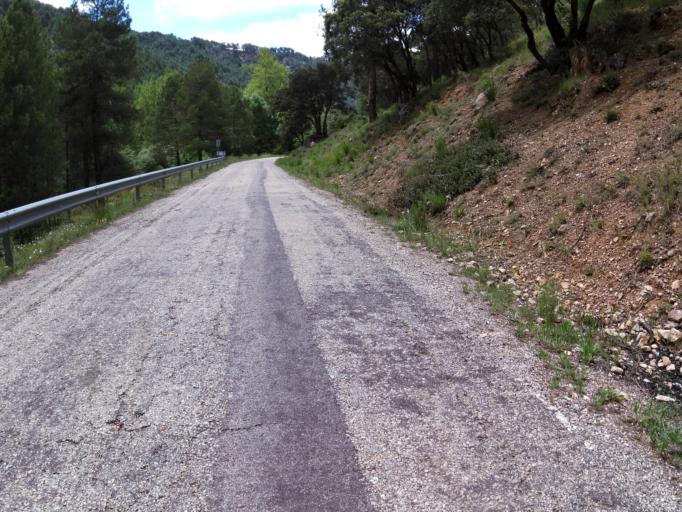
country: ES
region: Castille-La Mancha
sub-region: Provincia de Albacete
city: Paterna del Madera
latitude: 38.5757
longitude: -2.3535
